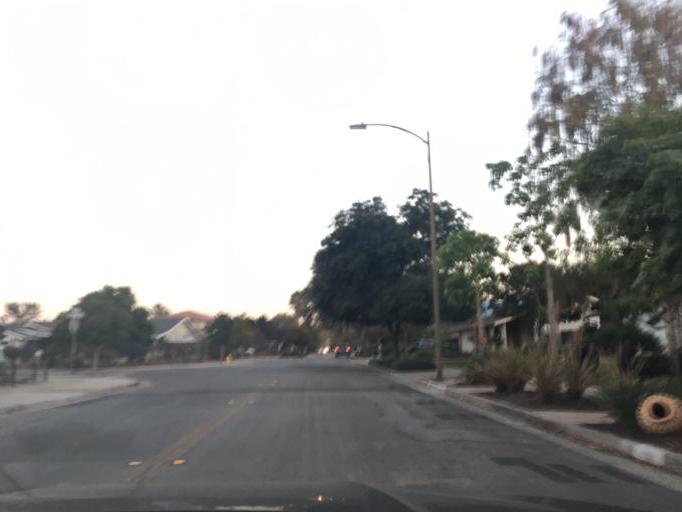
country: US
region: California
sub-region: Santa Clara County
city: Cambrian Park
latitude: 37.2272
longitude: -121.8722
